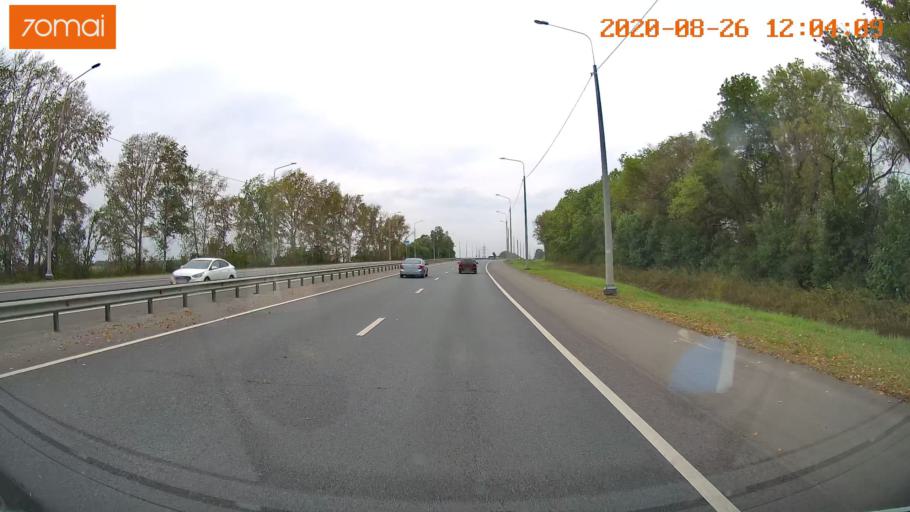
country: RU
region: Rjazan
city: Kiritsy
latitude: 54.3070
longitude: 40.1938
